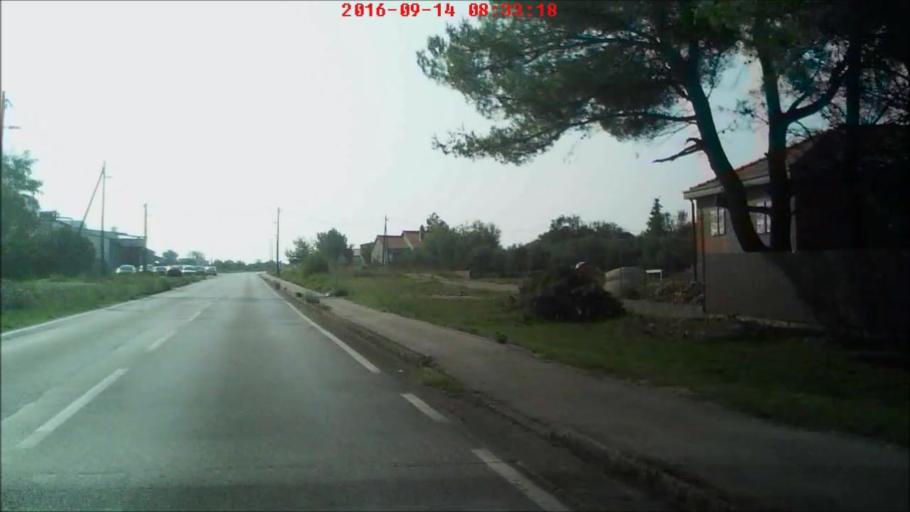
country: HR
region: Zadarska
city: Policnik
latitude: 44.1573
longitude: 15.3113
